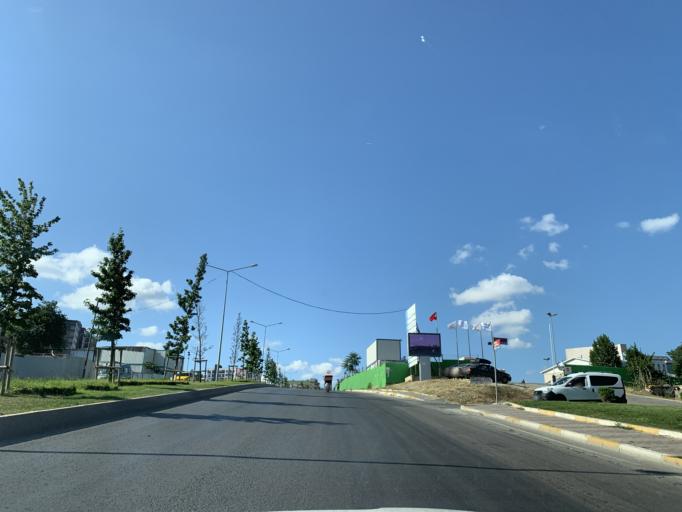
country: TR
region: Istanbul
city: Pendik
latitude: 40.8828
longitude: 29.2596
